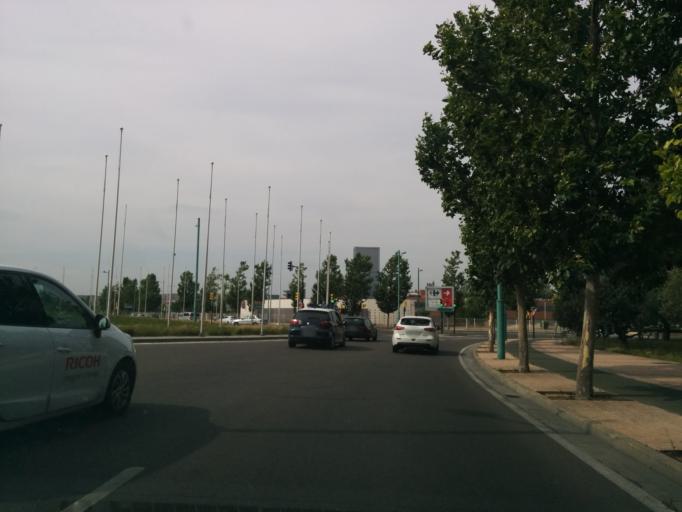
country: ES
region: Aragon
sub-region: Provincia de Zaragoza
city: Almozara
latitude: 41.6712
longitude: -0.8969
